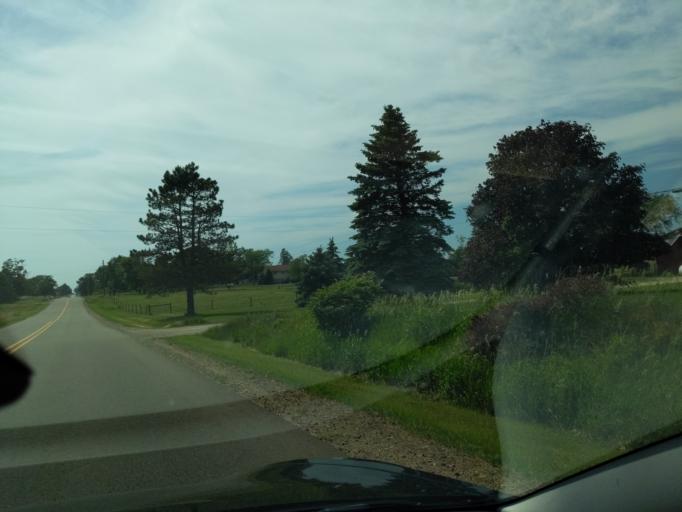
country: US
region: Michigan
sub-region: Eaton County
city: Grand Ledge
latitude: 42.7121
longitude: -84.8387
